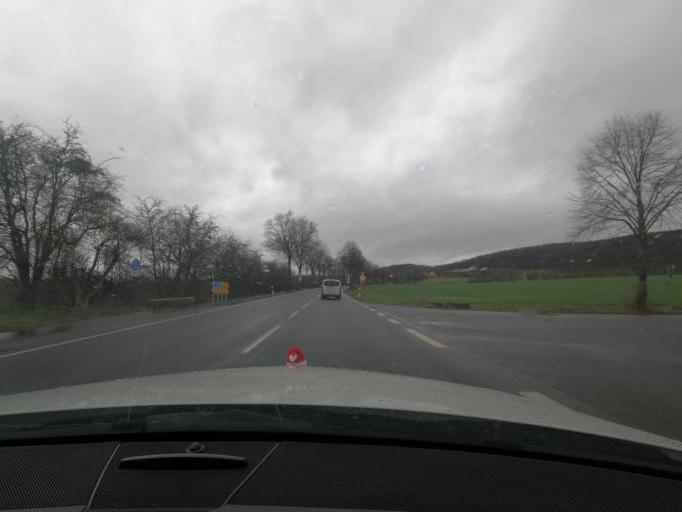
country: DE
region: Lower Saxony
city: Einbeck
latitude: 51.7861
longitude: 9.9334
